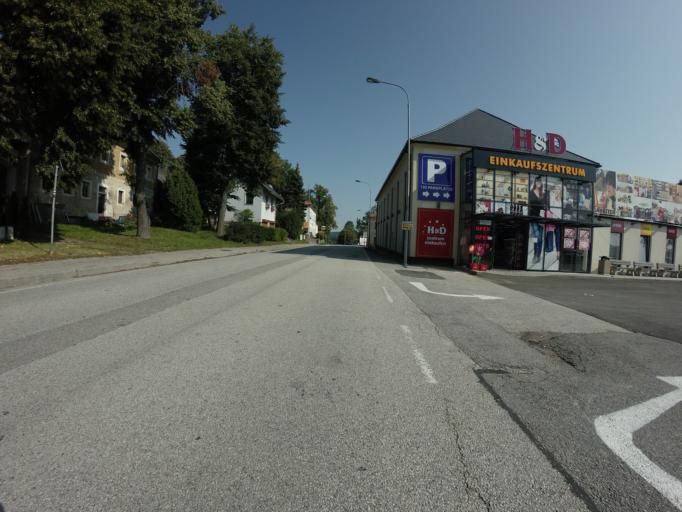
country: CZ
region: Jihocesky
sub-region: Okres Cesky Krumlov
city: Vyssi Brod
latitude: 48.5896
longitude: 14.3260
